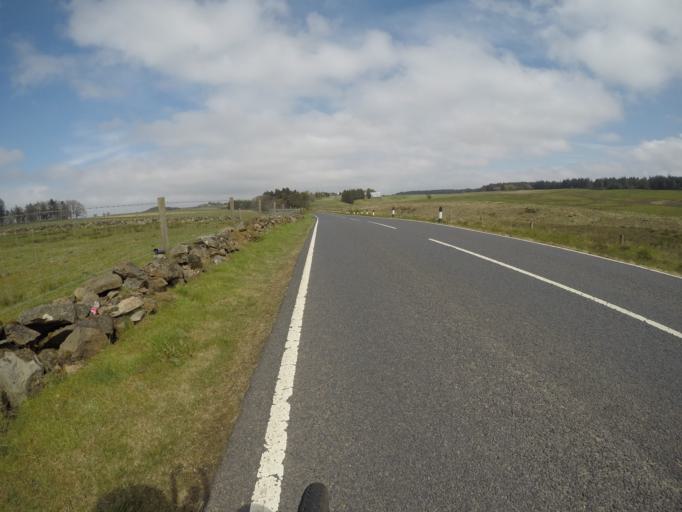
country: GB
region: Scotland
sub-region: East Renfrewshire
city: Neilston
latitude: 55.7171
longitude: -4.4373
